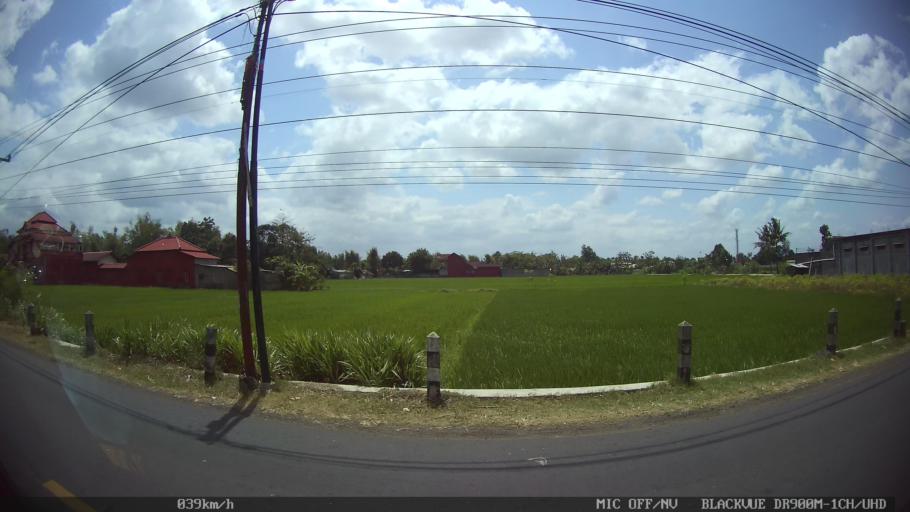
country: ID
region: Daerah Istimewa Yogyakarta
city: Bantul
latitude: -7.9092
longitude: 110.3495
